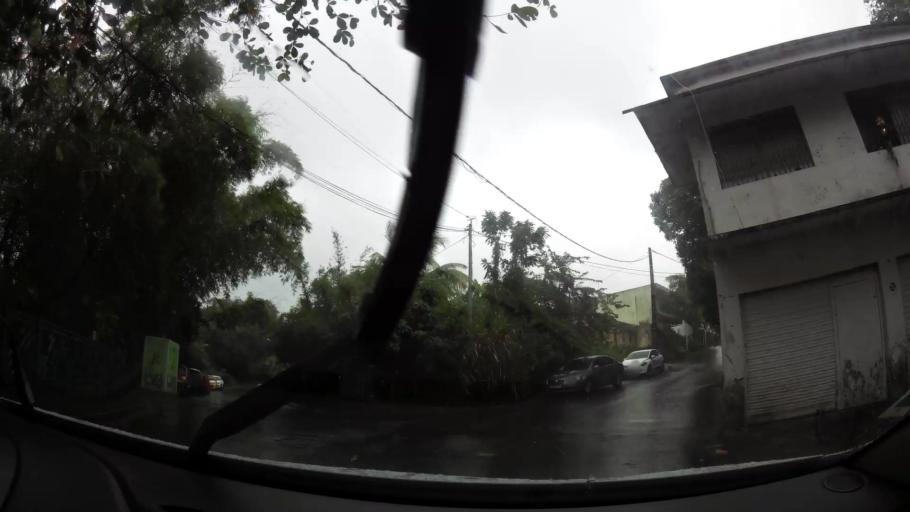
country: RE
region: Reunion
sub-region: Reunion
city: Saint-Andre
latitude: -20.9644
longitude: 55.6488
